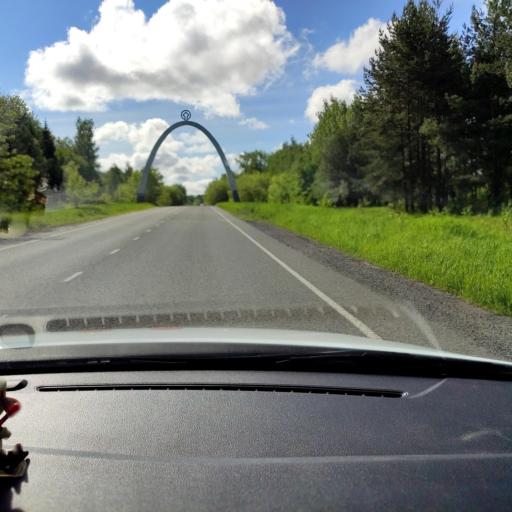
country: RU
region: Tatarstan
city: Stolbishchi
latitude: 55.7237
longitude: 49.2033
